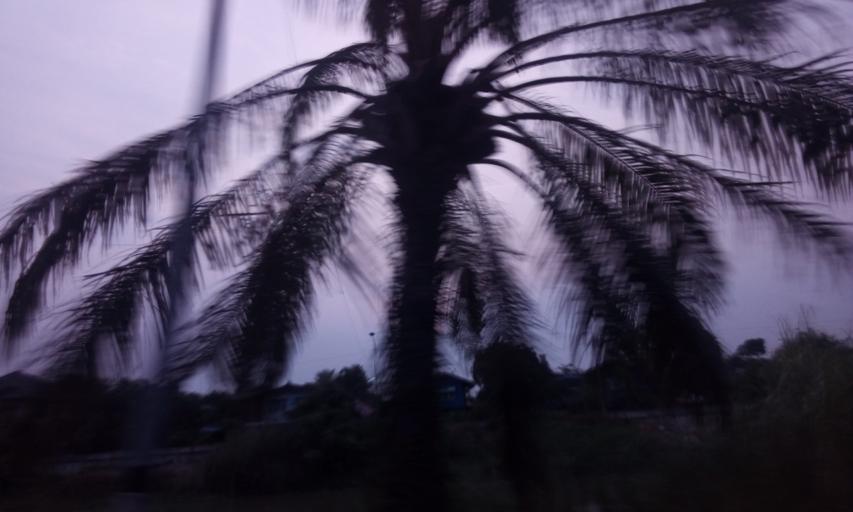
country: TH
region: Pathum Thani
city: Ban Lam Luk Ka
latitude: 14.0161
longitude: 100.8944
